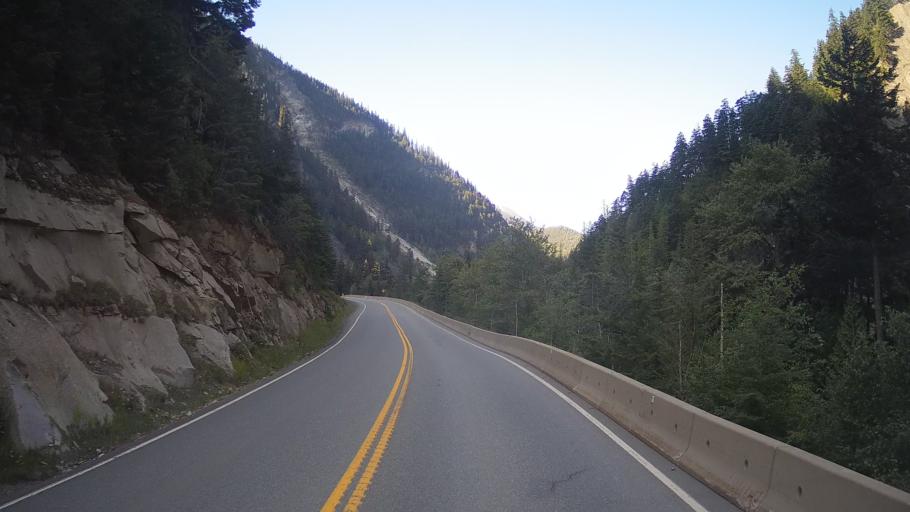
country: CA
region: British Columbia
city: Lillooet
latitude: 50.5472
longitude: -122.1060
